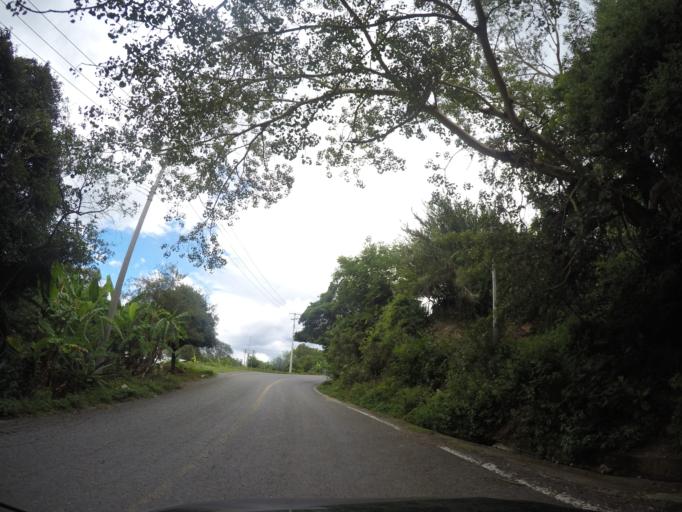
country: MX
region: Oaxaca
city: San Francisco Sola
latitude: 16.4899
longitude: -96.9848
